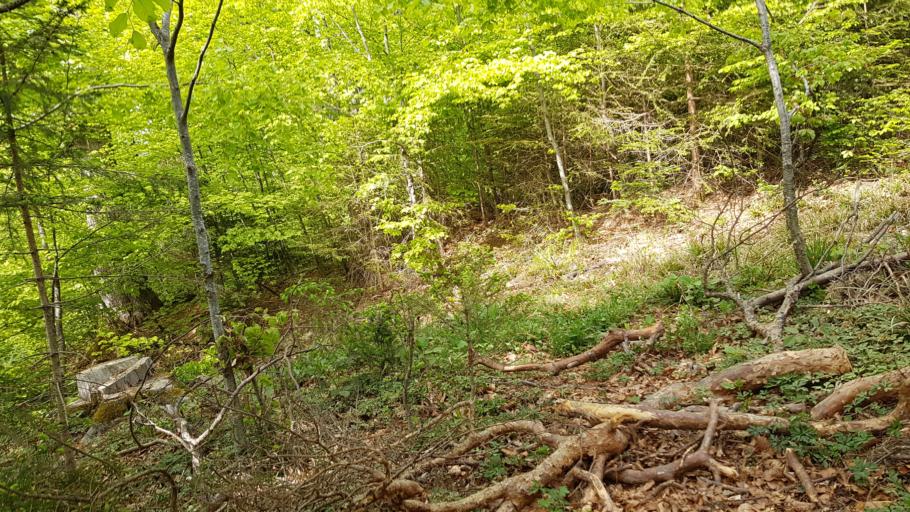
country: CH
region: Aargau
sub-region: Bezirk Kulm
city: Reinach
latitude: 47.2860
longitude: 8.1754
